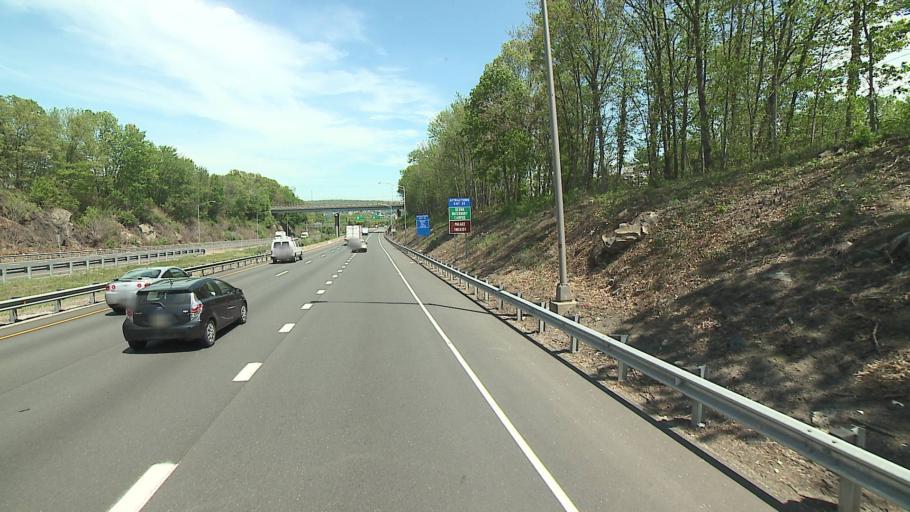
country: US
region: Connecticut
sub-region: New Haven County
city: Waterbury
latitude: 41.5493
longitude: -73.0609
